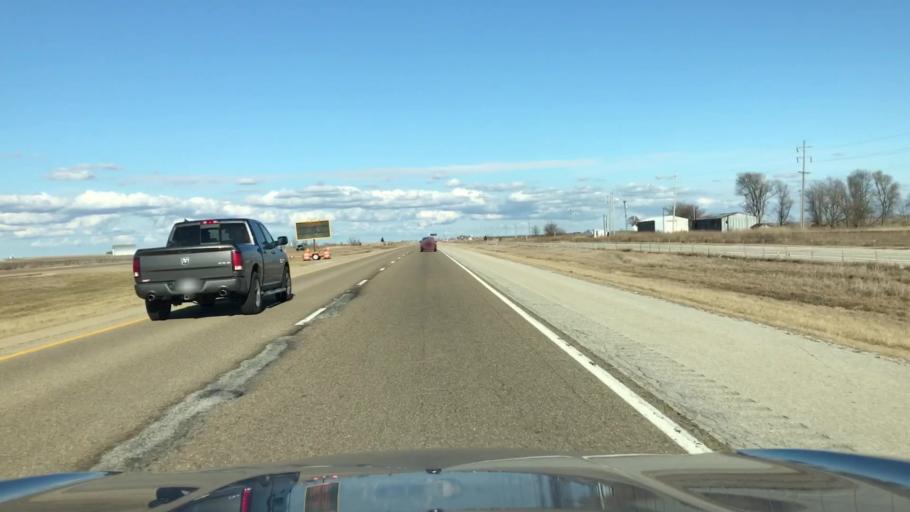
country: US
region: Illinois
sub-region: McLean County
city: Lexington
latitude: 40.6890
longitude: -88.7562
